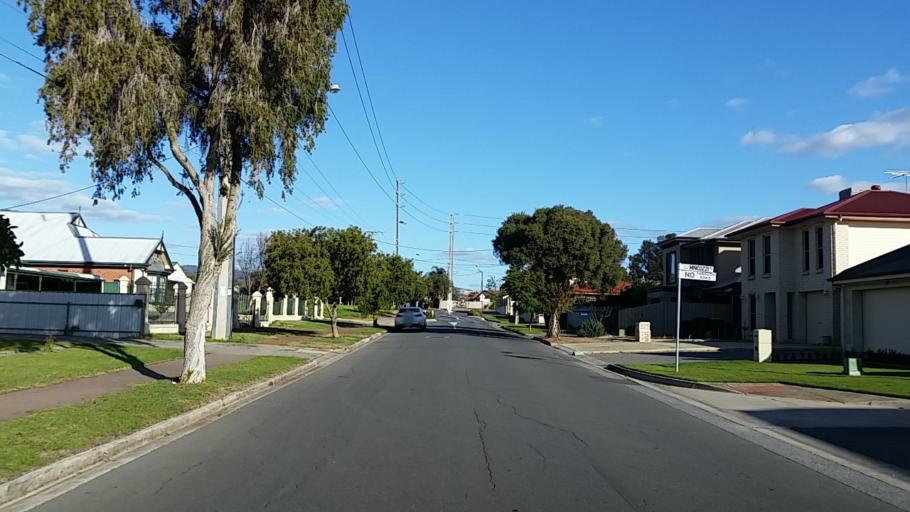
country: AU
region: South Australia
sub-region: Campbelltown
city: Paradise
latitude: -34.8747
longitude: 138.6800
